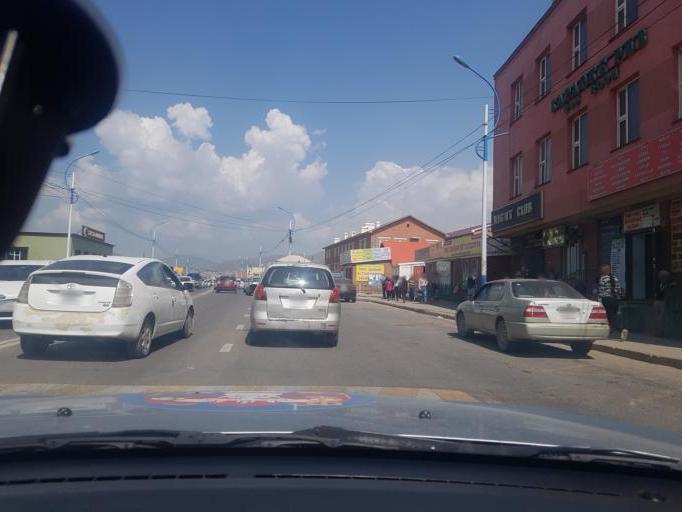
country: MN
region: Ulaanbaatar
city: Ulaanbaatar
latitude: 47.9538
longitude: 106.8263
